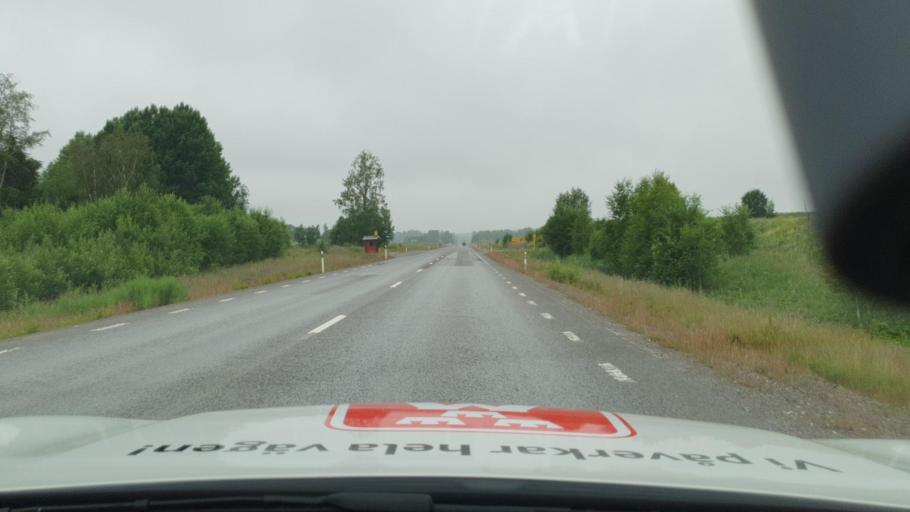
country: SE
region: Vaermland
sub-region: Karlstads Kommun
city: Edsvalla
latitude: 59.5647
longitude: 13.1845
